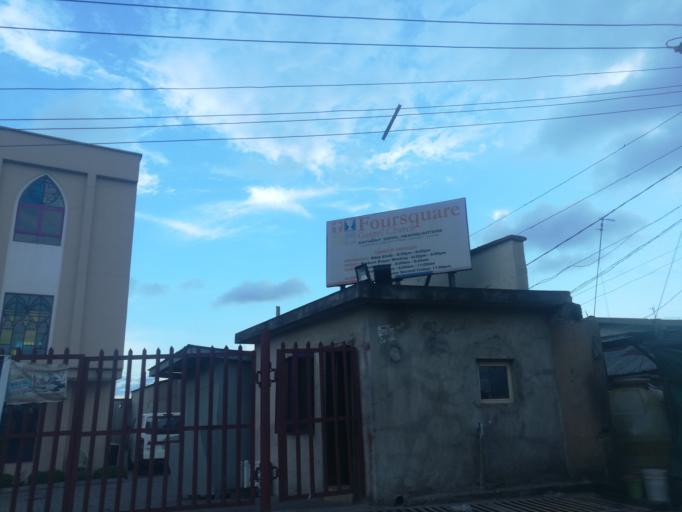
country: NG
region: Lagos
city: Somolu
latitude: 6.5586
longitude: 3.3705
